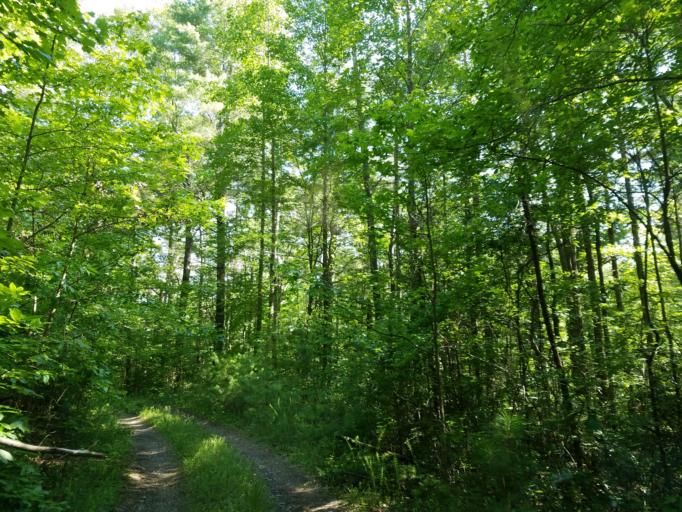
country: US
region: Georgia
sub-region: Dawson County
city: Dawsonville
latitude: 34.5806
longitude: -84.1777
